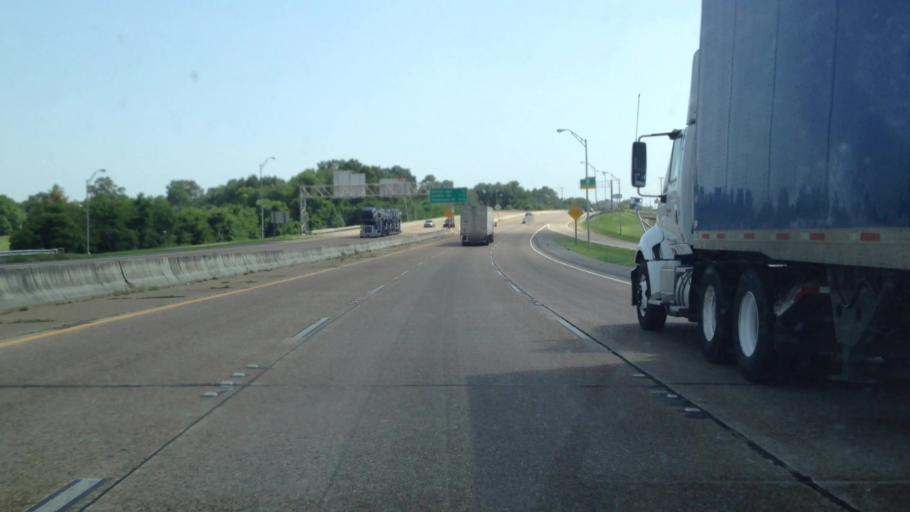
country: US
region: Louisiana
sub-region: Caddo Parish
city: Shreveport
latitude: 32.4849
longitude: -93.7743
